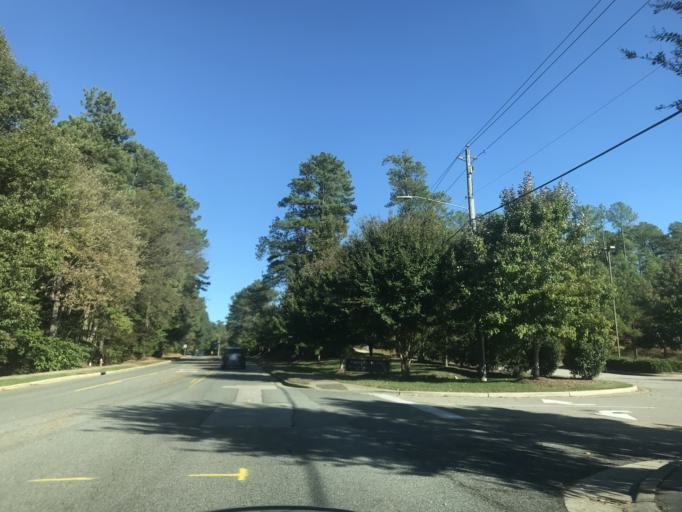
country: US
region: North Carolina
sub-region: Wake County
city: West Raleigh
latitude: 35.8784
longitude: -78.6411
